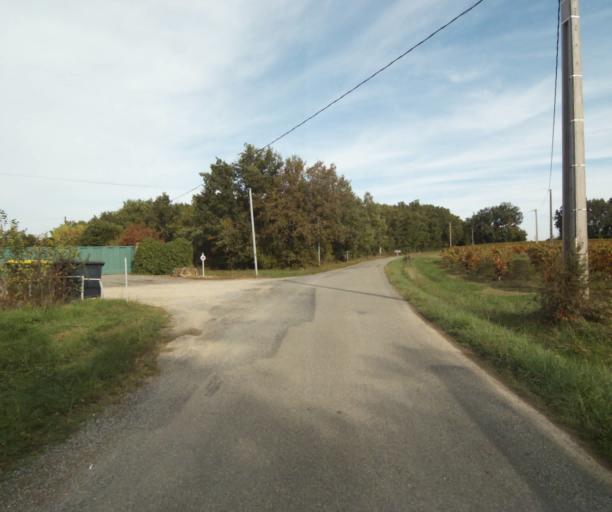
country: FR
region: Midi-Pyrenees
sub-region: Departement du Tarn-et-Garonne
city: Orgueil
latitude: 43.8902
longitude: 1.4030
